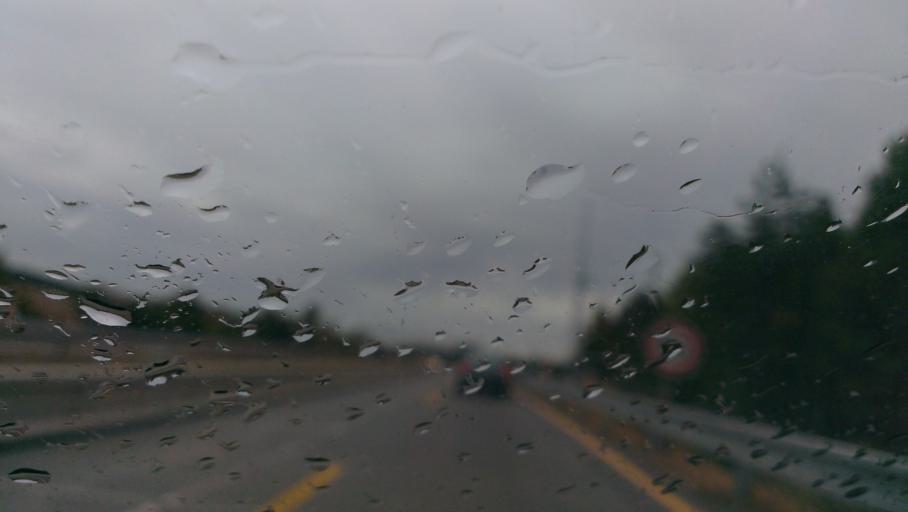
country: CZ
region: South Moravian
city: Ricany
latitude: 49.1922
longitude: 16.4364
